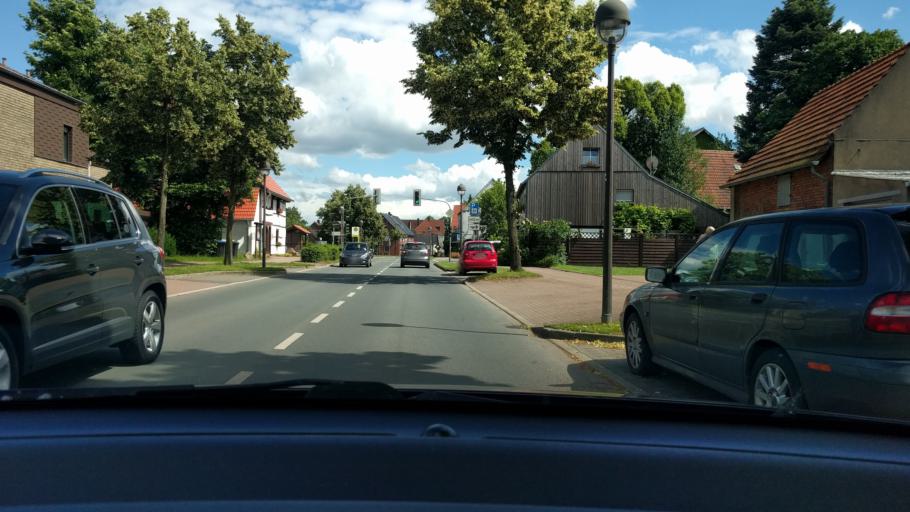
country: DE
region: North Rhine-Westphalia
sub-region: Regierungsbezirk Munster
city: Haltern
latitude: 51.7195
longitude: 7.2317
